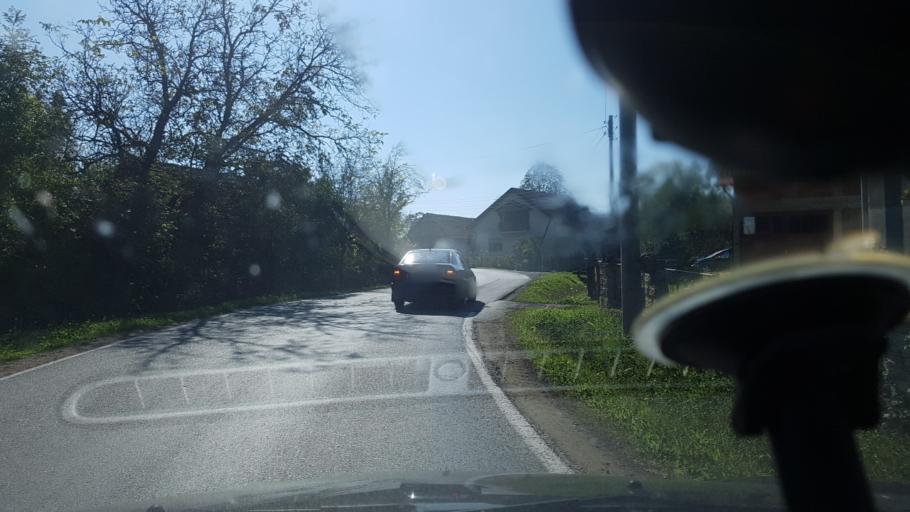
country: HR
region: Zagrebacka
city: Lupoglav
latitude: 45.7187
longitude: 16.3125
